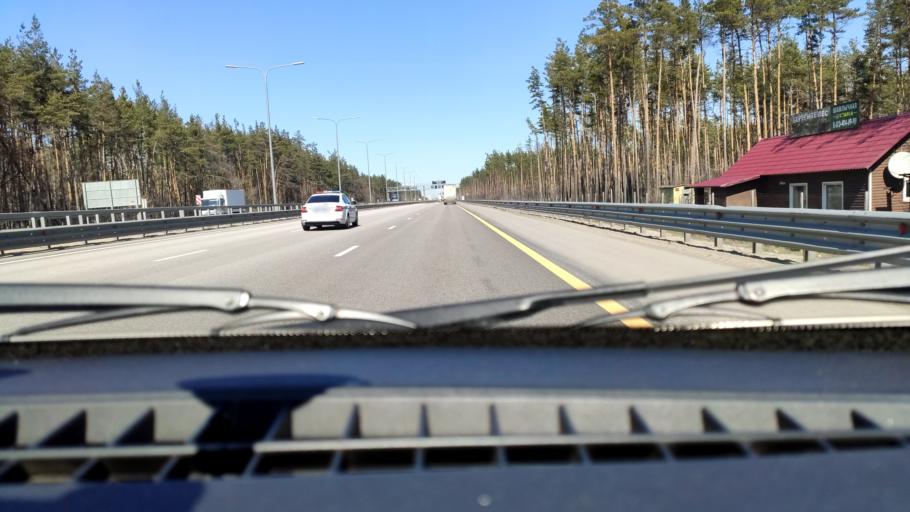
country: RU
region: Voronezj
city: Somovo
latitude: 51.6988
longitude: 39.3053
